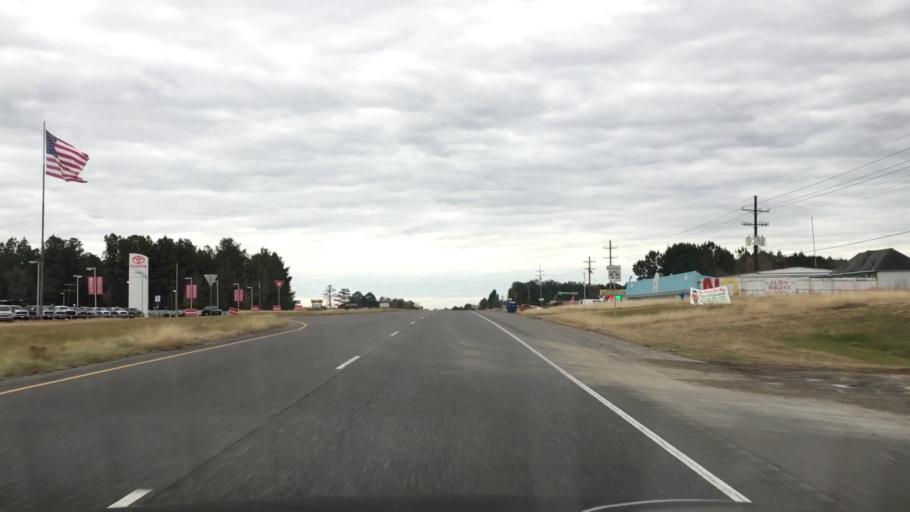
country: US
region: Louisiana
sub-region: Vernon Parish
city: New Llano
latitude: 31.0888
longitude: -93.2711
